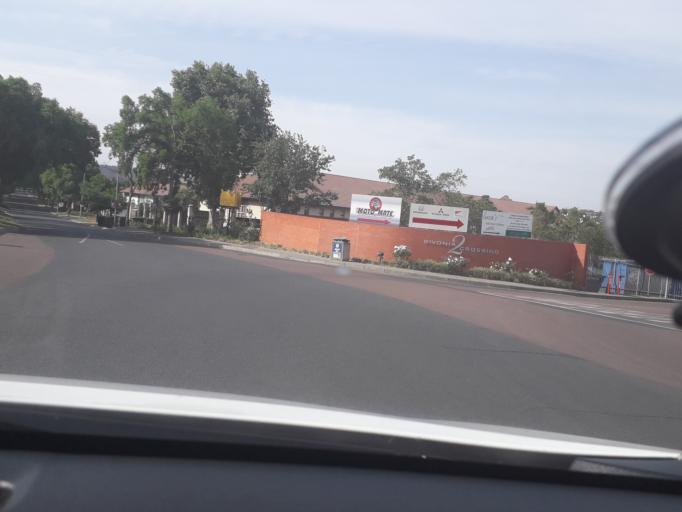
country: ZA
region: Gauteng
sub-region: City of Johannesburg Metropolitan Municipality
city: Midrand
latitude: -26.0367
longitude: 28.0584
